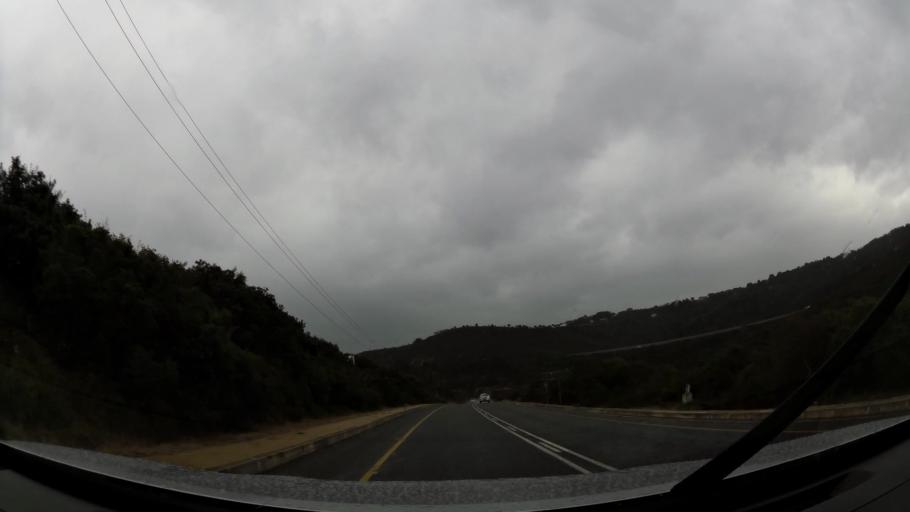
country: ZA
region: Western Cape
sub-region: Eden District Municipality
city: Mossel Bay
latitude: -34.0502
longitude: 22.2432
